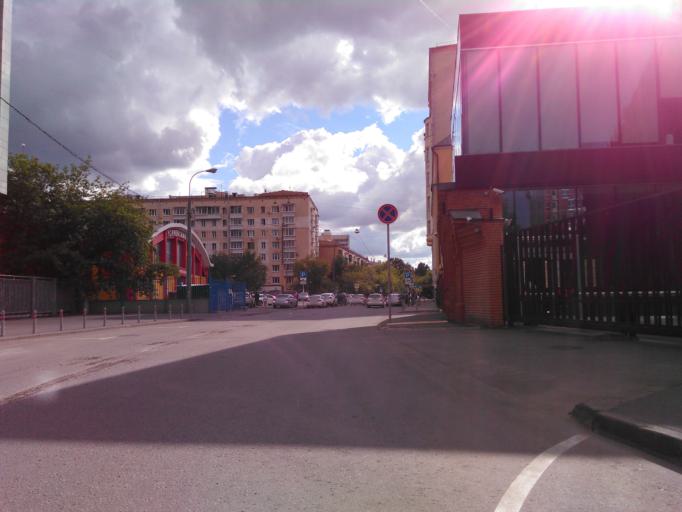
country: RU
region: Moscow
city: Luzhniki
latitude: 55.7283
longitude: 37.5683
